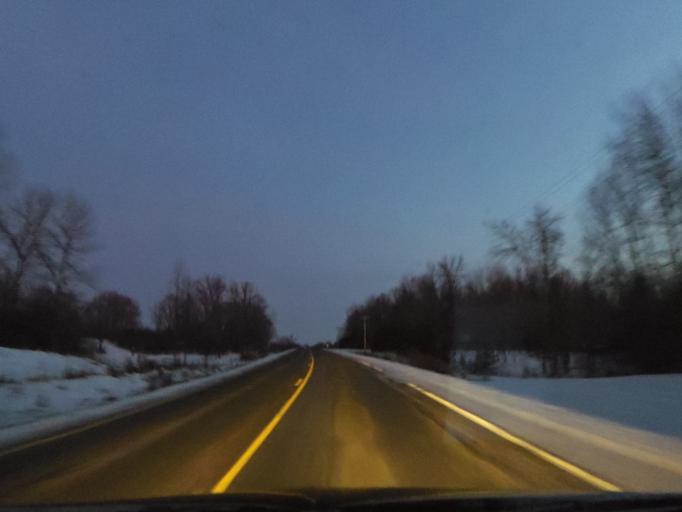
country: US
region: Minnesota
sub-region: Chisago County
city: Center City
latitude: 45.3720
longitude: -92.7906
